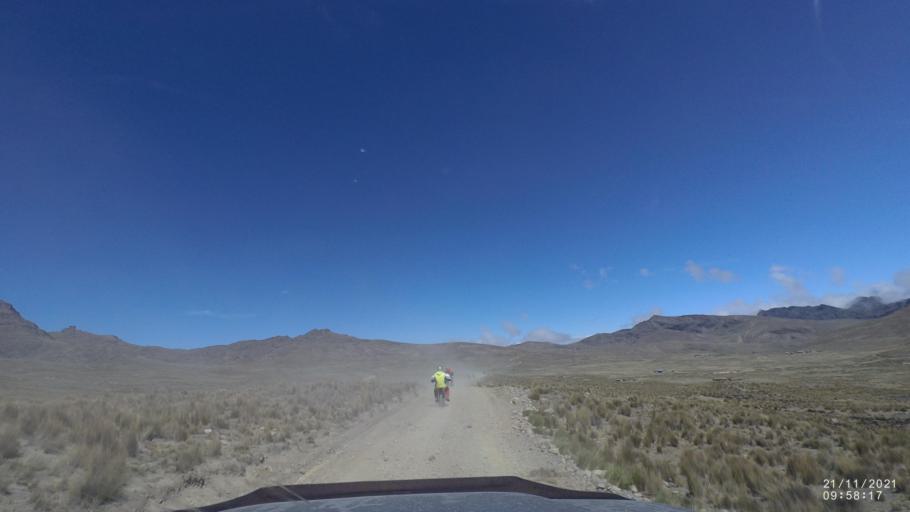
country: BO
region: Cochabamba
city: Cochabamba
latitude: -17.0370
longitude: -66.2758
